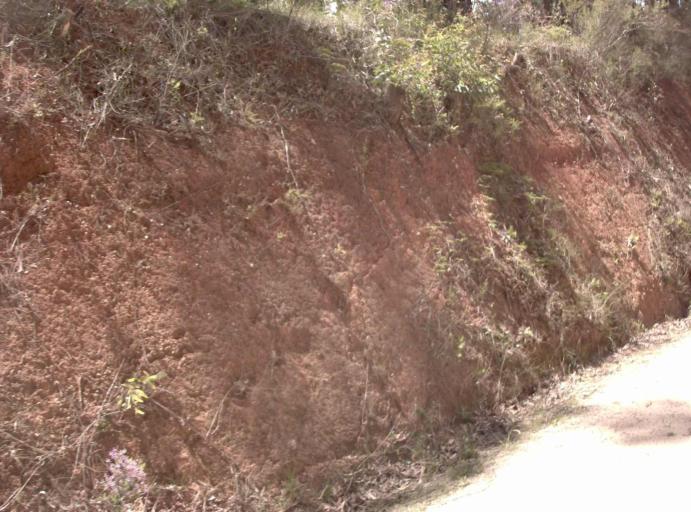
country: AU
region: New South Wales
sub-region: Bombala
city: Bombala
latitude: -37.5835
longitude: 149.0030
